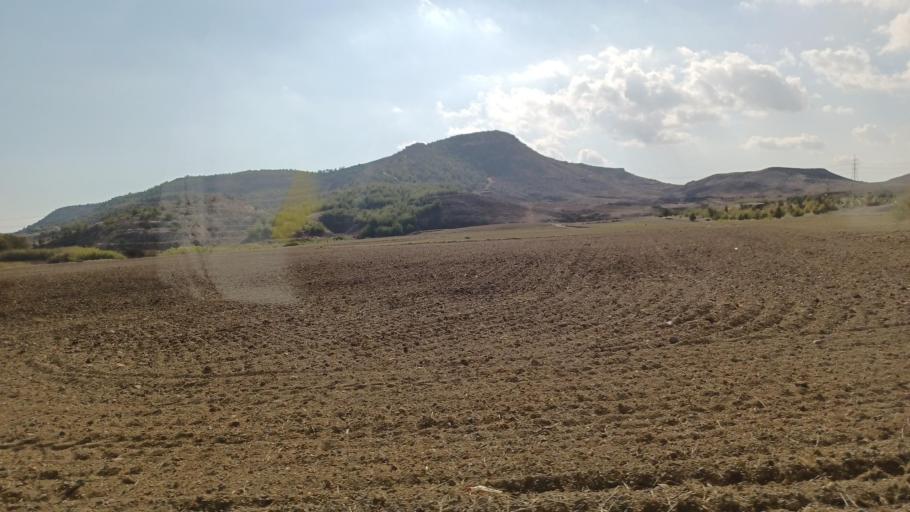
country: CY
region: Larnaka
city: Voroklini
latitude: 35.0087
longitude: 33.6444
